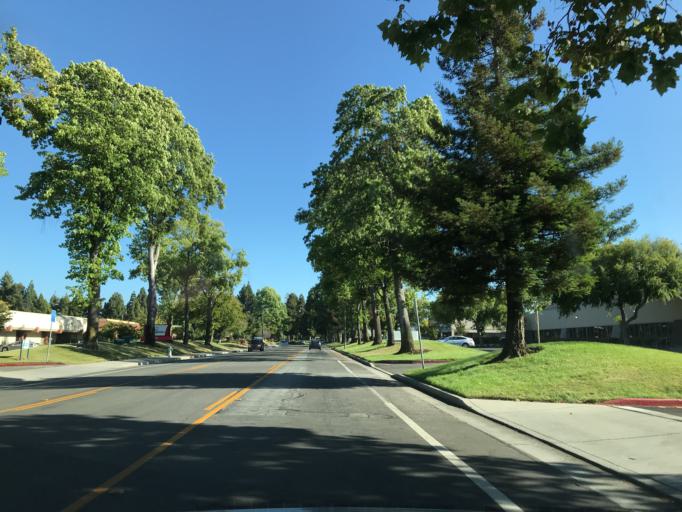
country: US
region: California
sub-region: Santa Clara County
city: Santa Clara
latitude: 37.3853
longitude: -121.9884
